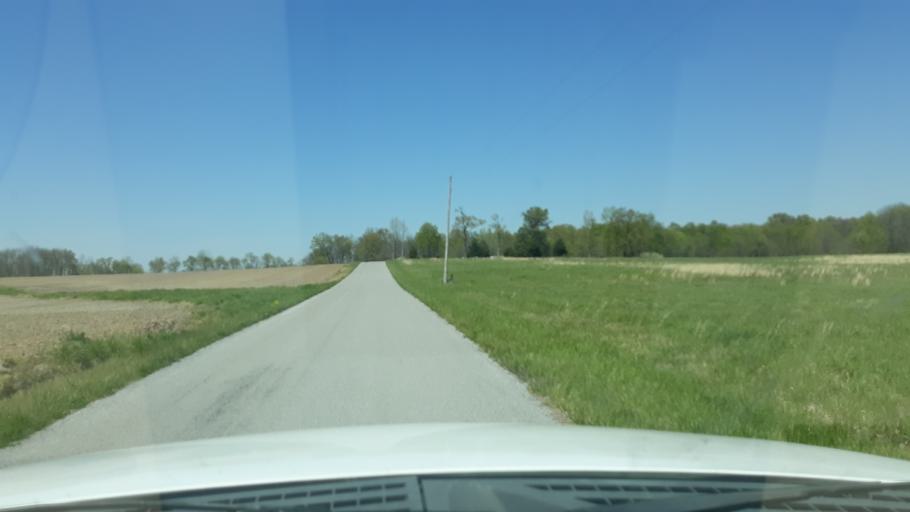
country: US
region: Illinois
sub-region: Saline County
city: Harrisburg
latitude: 37.8899
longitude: -88.6698
